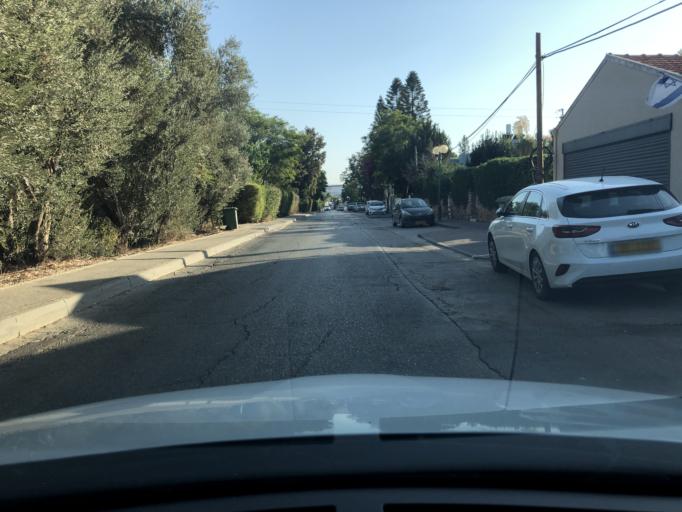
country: IL
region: Central District
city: Hod HaSharon
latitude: 32.1376
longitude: 34.9028
